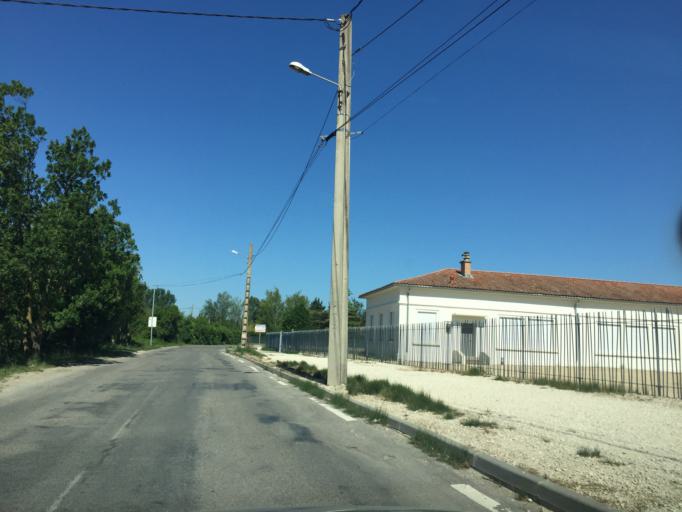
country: FR
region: Provence-Alpes-Cote d'Azur
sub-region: Departement du Vaucluse
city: L'Isle-sur-la-Sorgue
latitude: 43.9253
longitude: 5.0352
